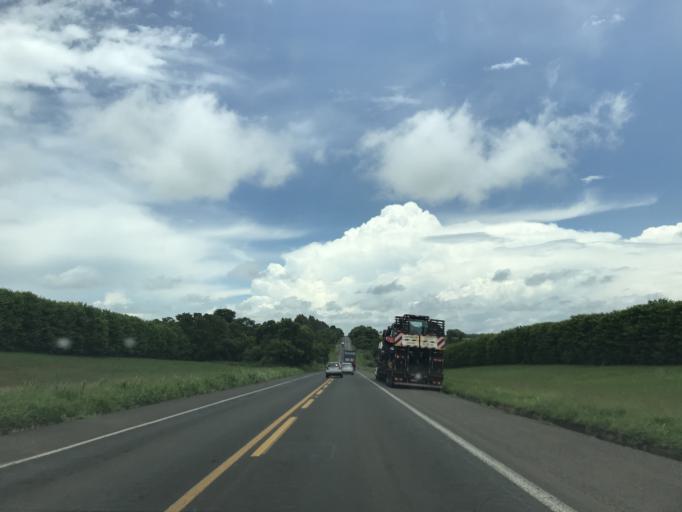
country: BR
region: Minas Gerais
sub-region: Frutal
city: Frutal
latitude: -19.7017
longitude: -48.9820
